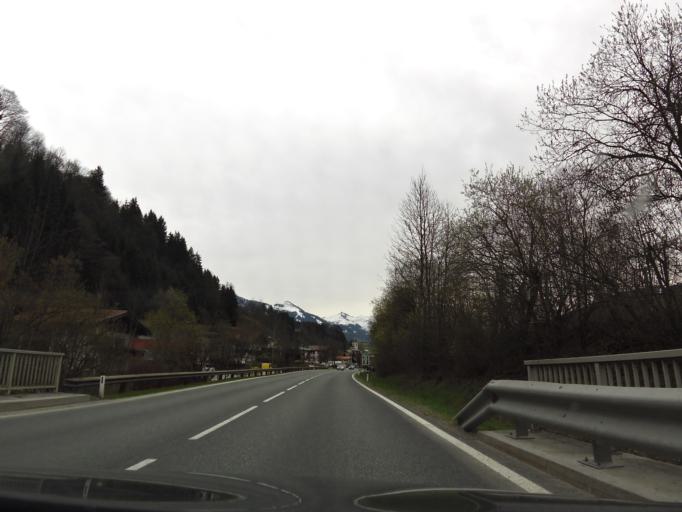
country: AT
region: Tyrol
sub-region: Politischer Bezirk Kitzbuhel
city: Itter
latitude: 47.4582
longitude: 12.1466
